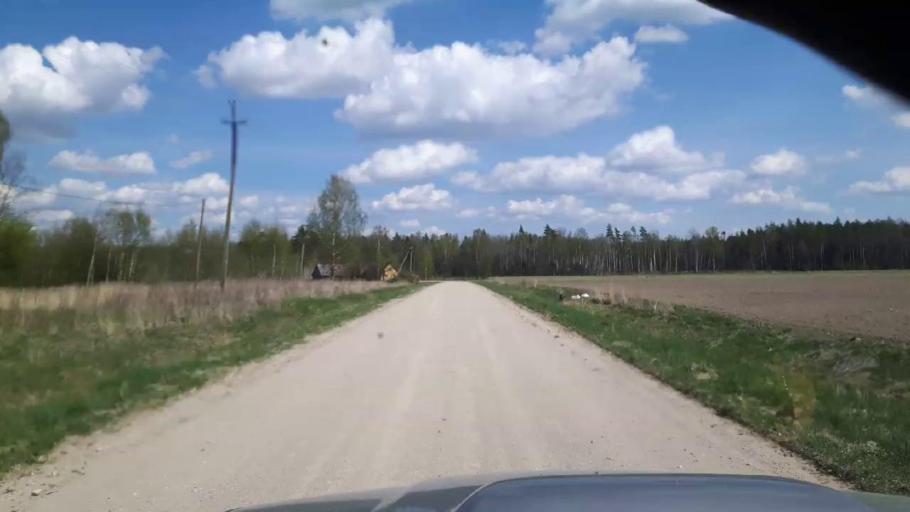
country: EE
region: Paernumaa
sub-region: Tootsi vald
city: Tootsi
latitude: 58.4735
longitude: 24.9032
